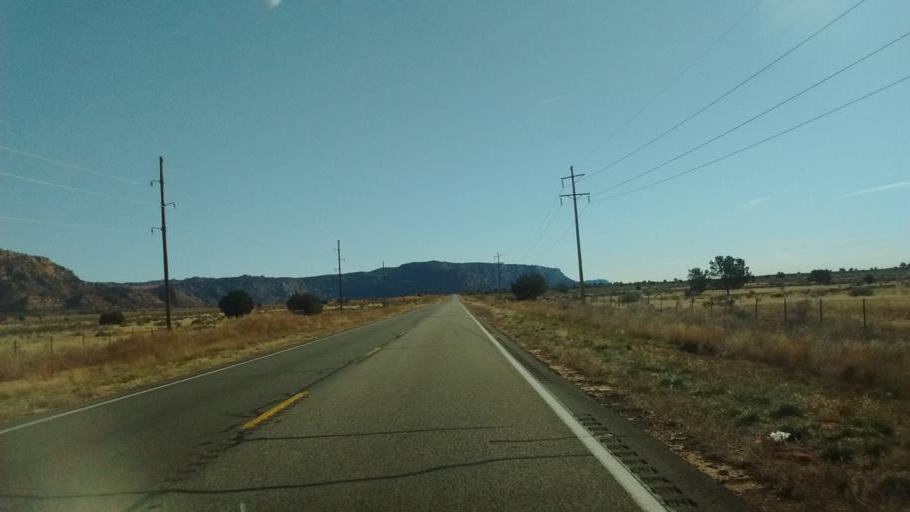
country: US
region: Arizona
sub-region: Mohave County
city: Colorado City
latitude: 37.0142
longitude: -113.0230
